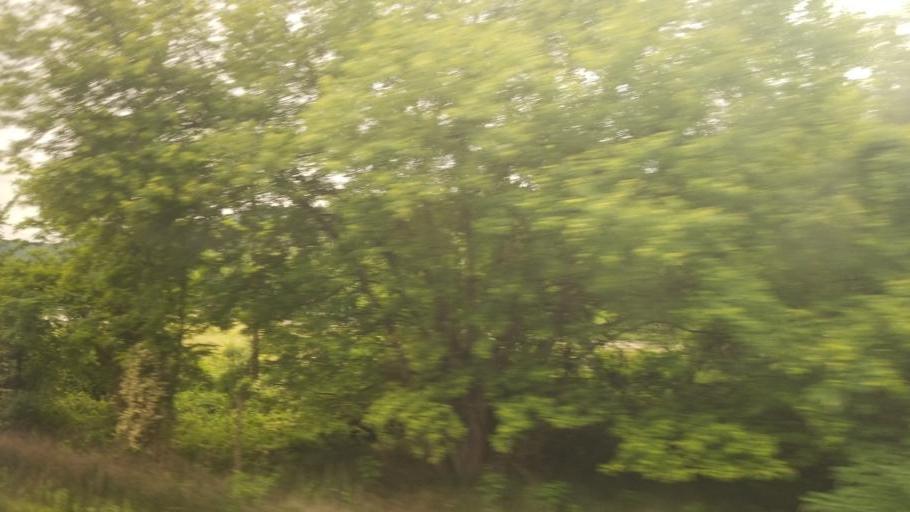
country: US
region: Maryland
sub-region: Allegany County
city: Cumberland
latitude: 39.6833
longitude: -78.7839
